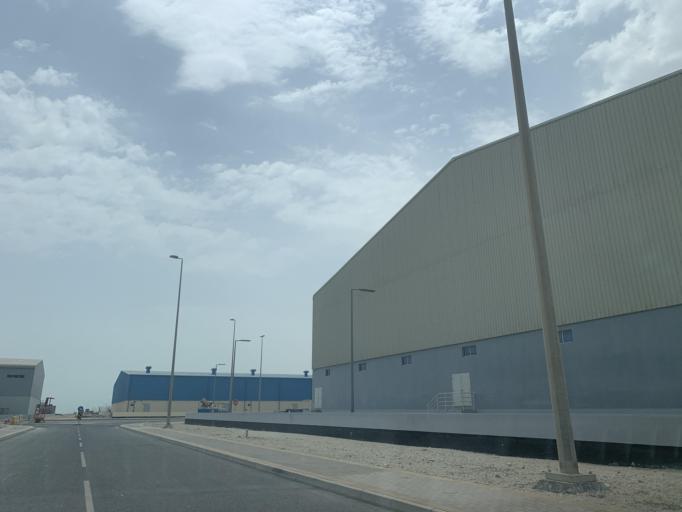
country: BH
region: Muharraq
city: Al Hadd
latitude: 26.2219
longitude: 50.6903
